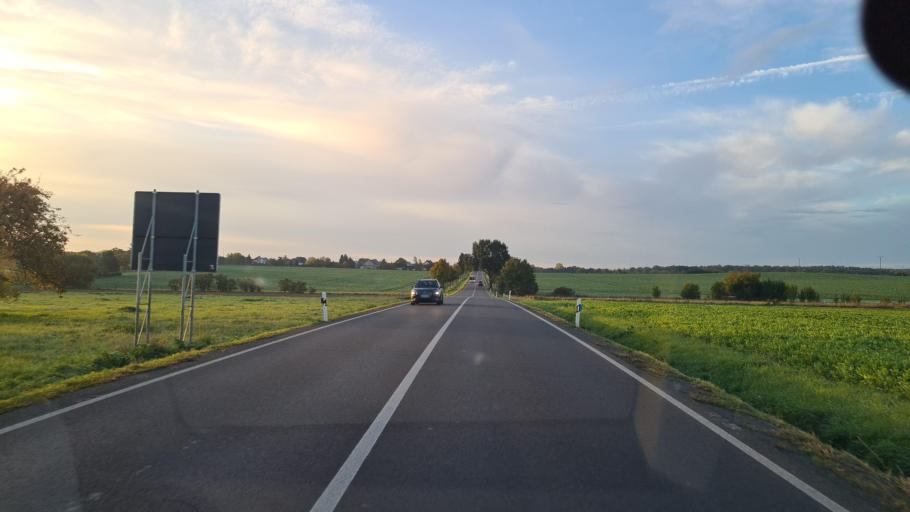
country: DE
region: Saxony
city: Machern
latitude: 51.3947
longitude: 12.6495
